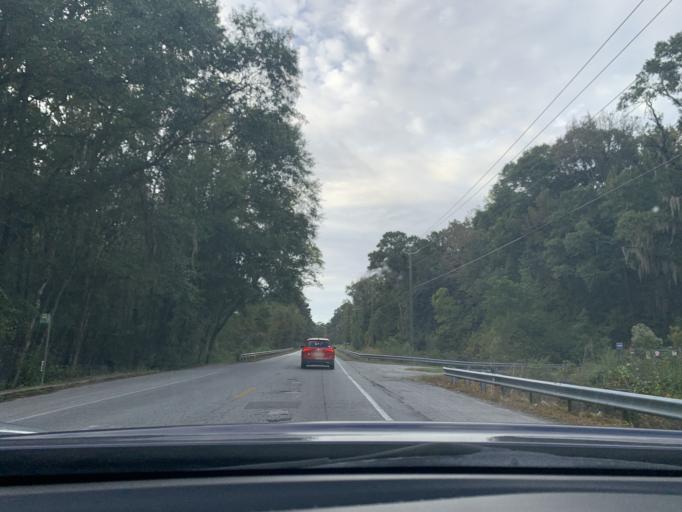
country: US
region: Georgia
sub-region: Chatham County
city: Georgetown
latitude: 32.0307
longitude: -81.2504
